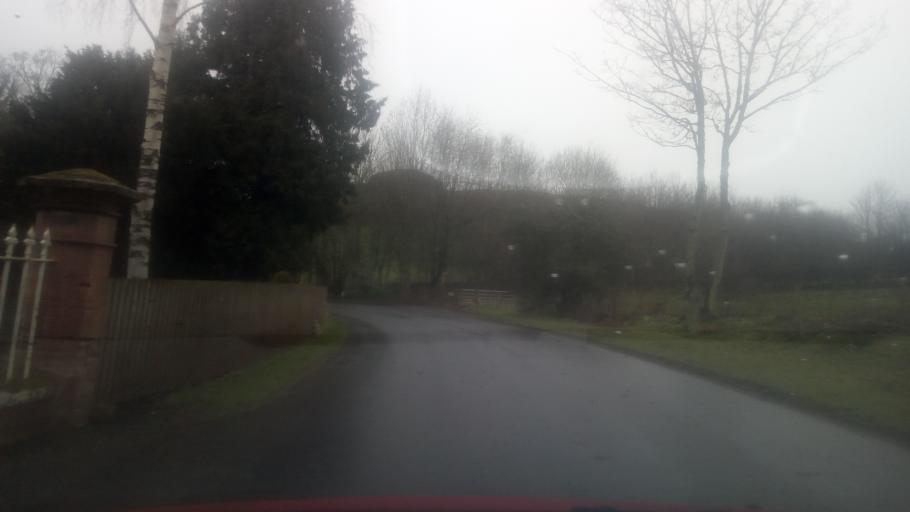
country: GB
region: Scotland
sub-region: The Scottish Borders
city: Earlston
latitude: 55.6266
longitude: -2.6688
